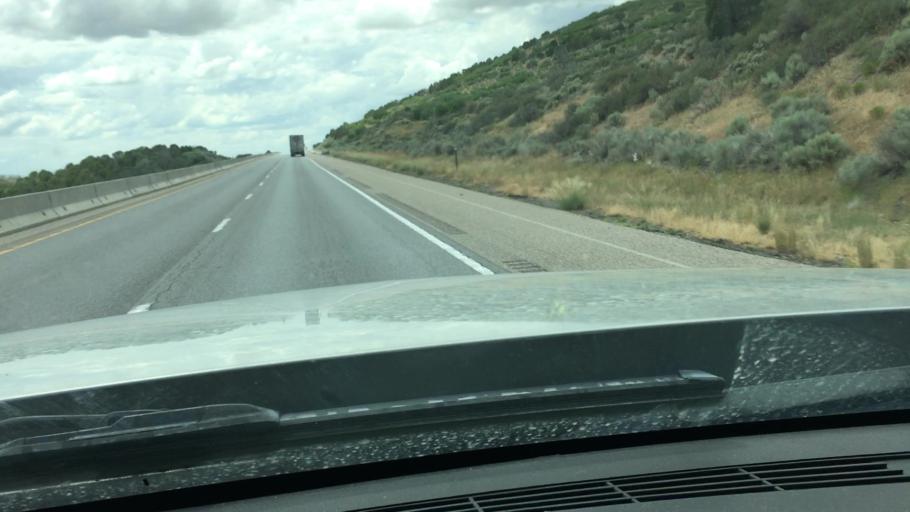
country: US
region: Utah
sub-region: Beaver County
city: Beaver
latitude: 38.4558
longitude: -112.6237
